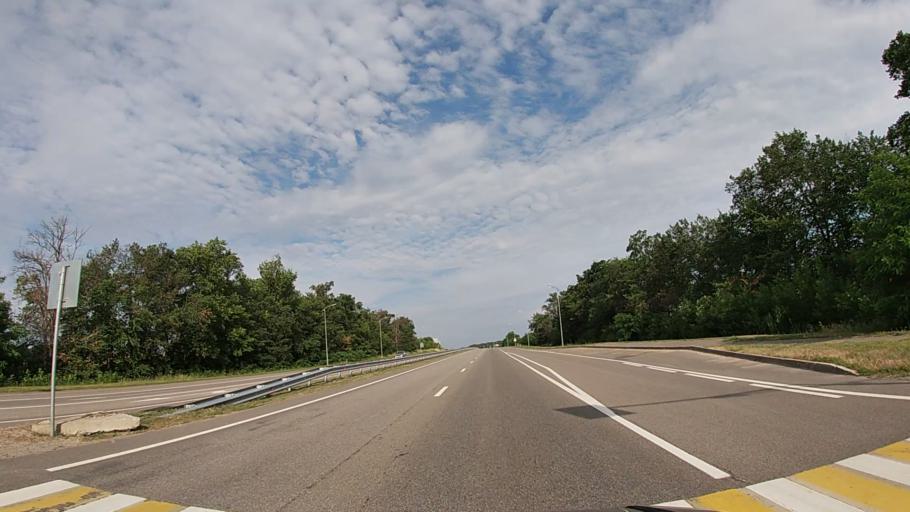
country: RU
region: Belgorod
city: Tomarovka
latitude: 50.6603
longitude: 36.3540
